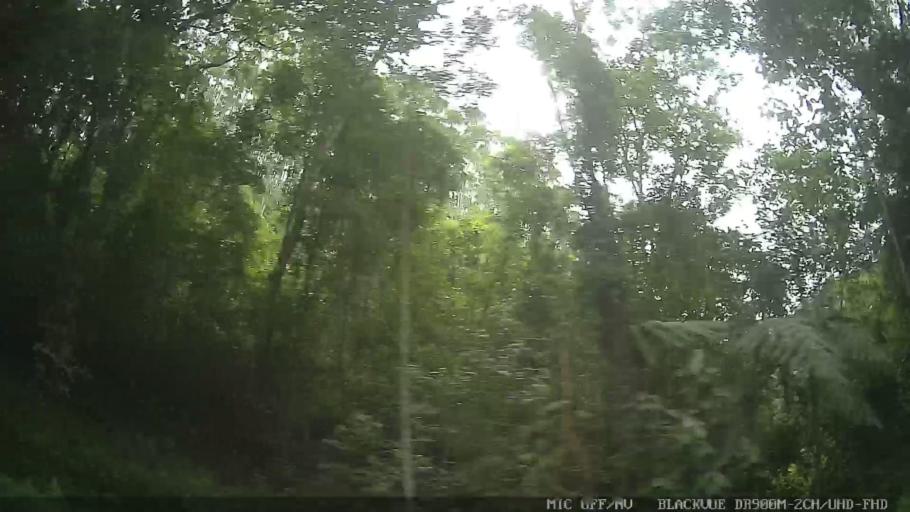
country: BR
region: Sao Paulo
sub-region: Santa Branca
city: Santa Branca
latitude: -23.5515
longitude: -45.6840
